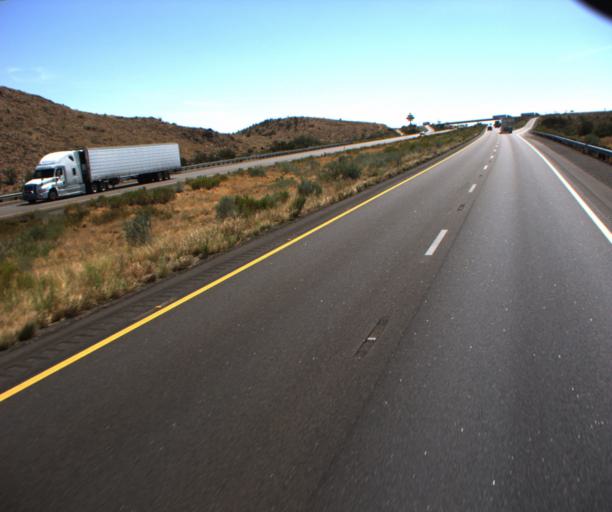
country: US
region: Arizona
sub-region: Mohave County
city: New Kingman-Butler
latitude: 35.1981
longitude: -113.9146
